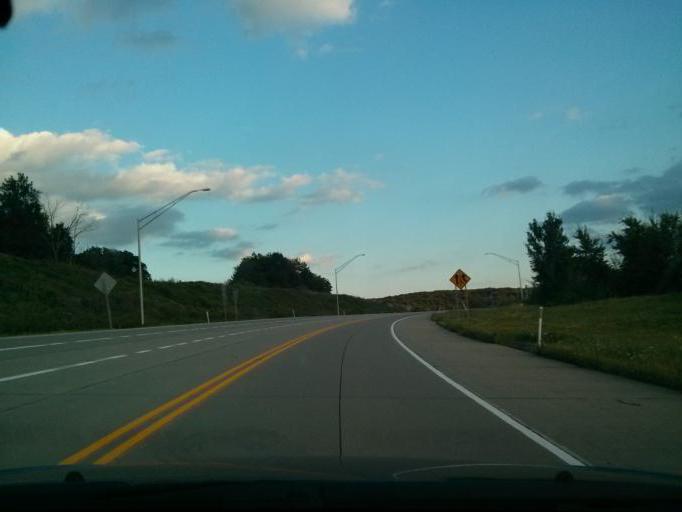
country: US
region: Pennsylvania
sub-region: Centre County
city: Park Forest Village
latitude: 40.8212
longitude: -77.9404
